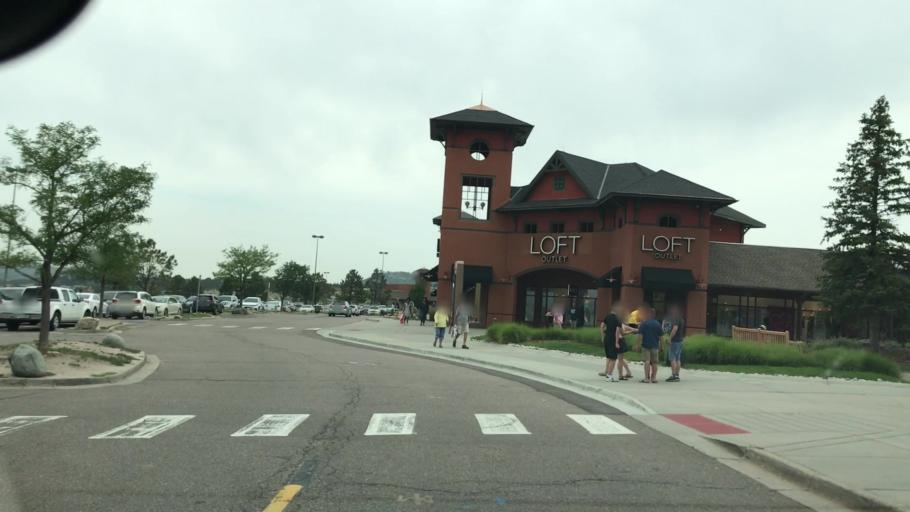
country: US
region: Colorado
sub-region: Douglas County
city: Castle Rock
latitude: 39.4142
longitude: -104.8734
